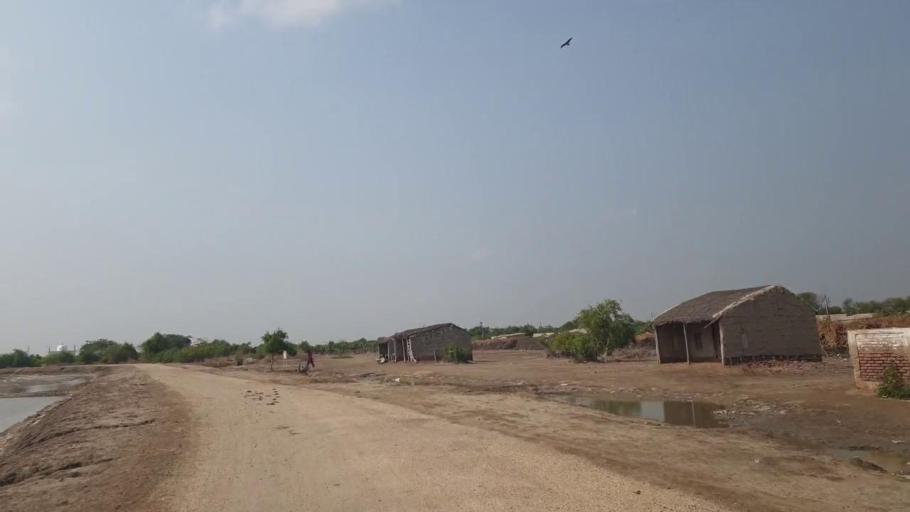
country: PK
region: Sindh
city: Badin
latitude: 24.5458
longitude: 68.6547
